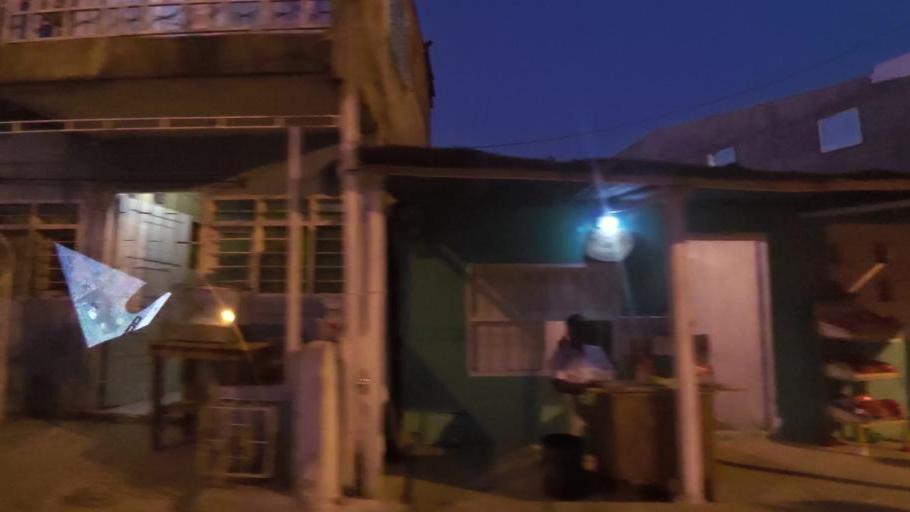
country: CO
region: Bolivar
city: Cartagena
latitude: 10.4024
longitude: -75.5094
